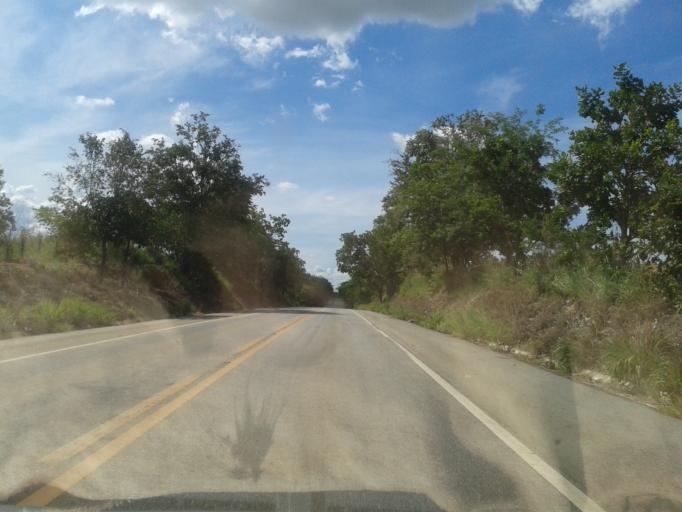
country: BR
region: Goias
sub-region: Itapuranga
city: Itapuranga
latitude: -15.4810
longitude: -50.3324
